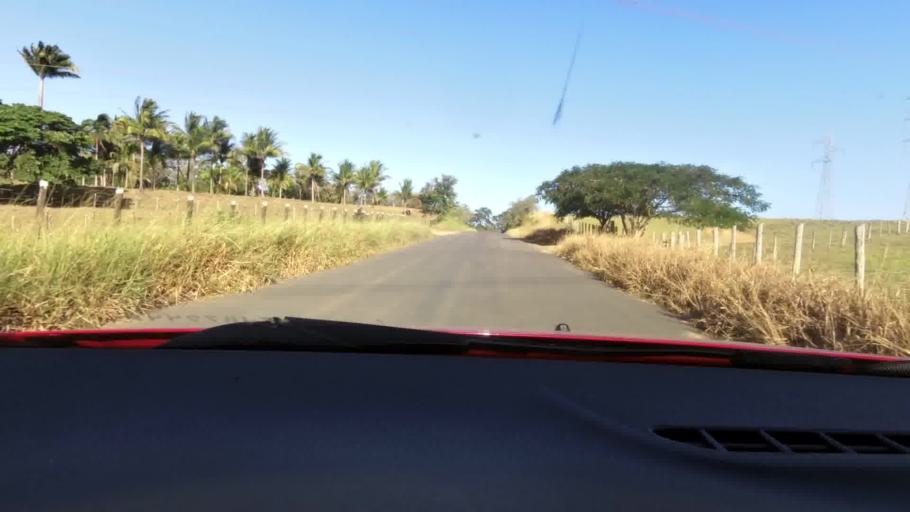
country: BR
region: Espirito Santo
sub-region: Guarapari
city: Guarapari
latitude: -20.5280
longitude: -40.4726
